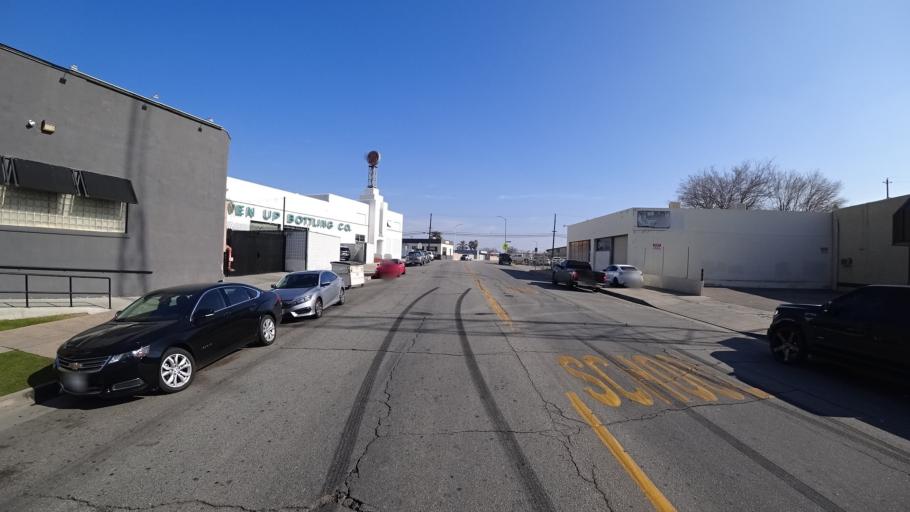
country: US
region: California
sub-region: Kern County
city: Bakersfield
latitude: 35.3753
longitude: -119.0010
